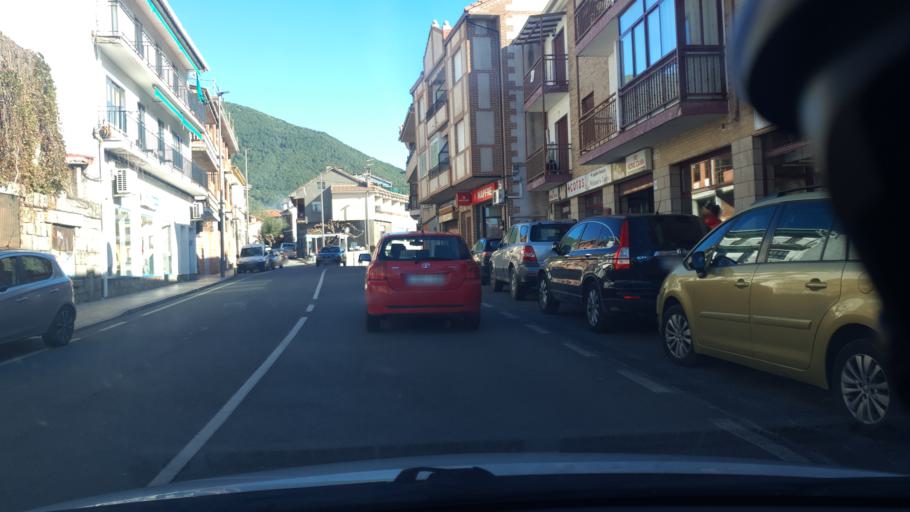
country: ES
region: Castille and Leon
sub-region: Provincia de Avila
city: Piedralaves
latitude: 40.3168
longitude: -4.6981
